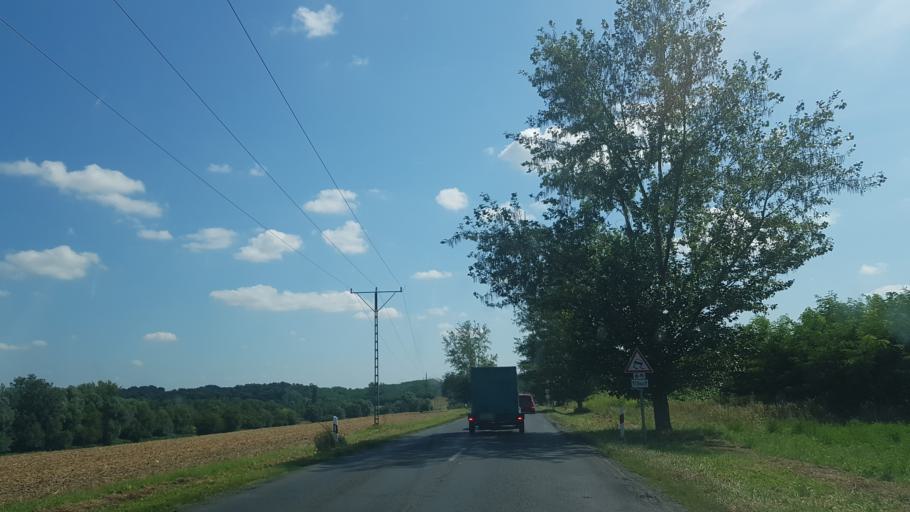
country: HU
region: Somogy
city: Bohonye
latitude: 46.4628
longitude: 17.3742
